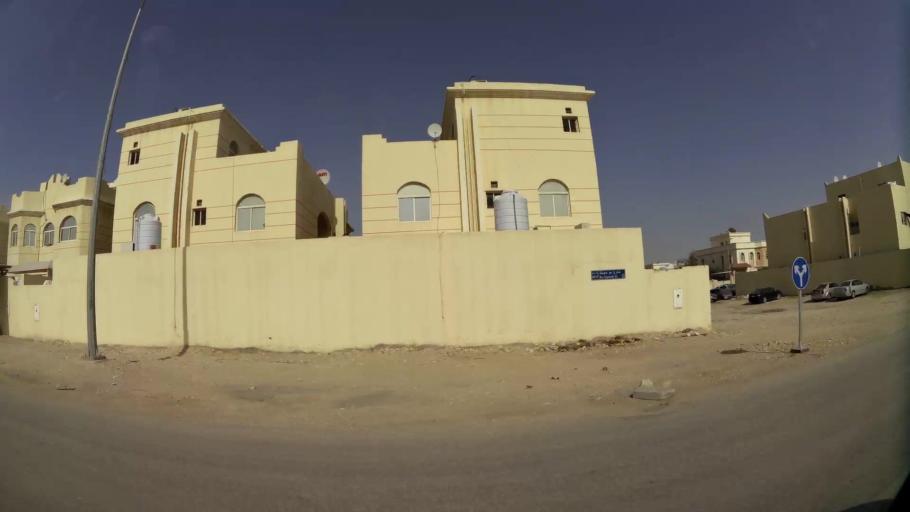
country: QA
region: Baladiyat ar Rayyan
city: Ar Rayyan
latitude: 25.3432
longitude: 51.4280
